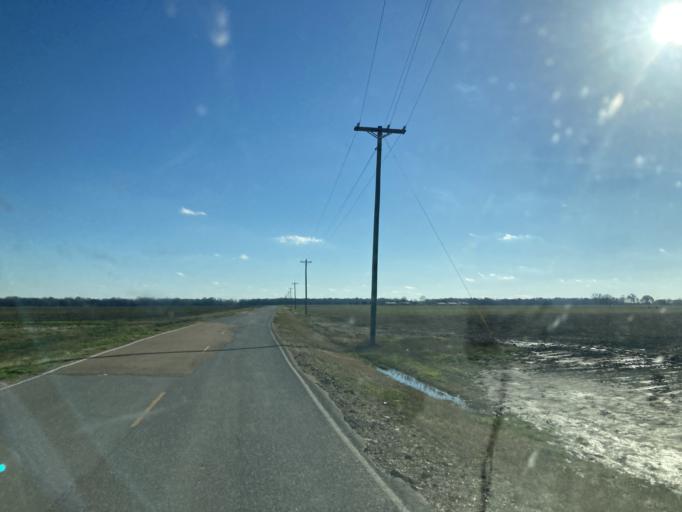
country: US
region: Mississippi
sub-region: Yazoo County
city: Yazoo City
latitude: 32.9317
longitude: -90.5058
